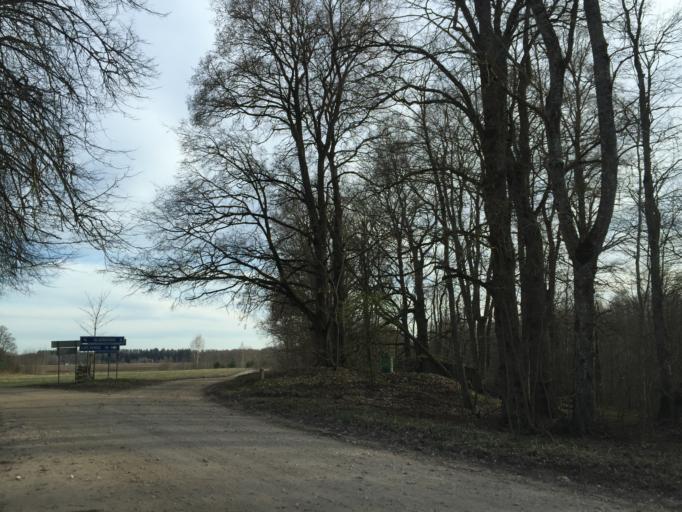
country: LV
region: Kegums
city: Kegums
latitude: 56.7988
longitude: 24.7490
